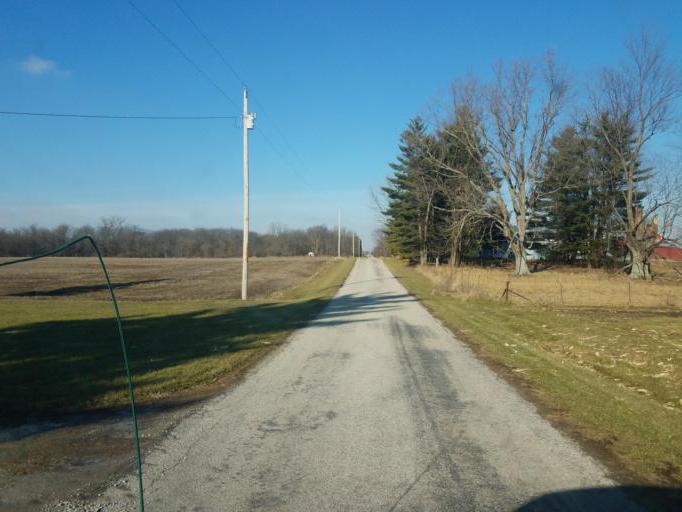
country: US
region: Ohio
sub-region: Wyandot County
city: Upper Sandusky
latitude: 40.6653
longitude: -83.3622
